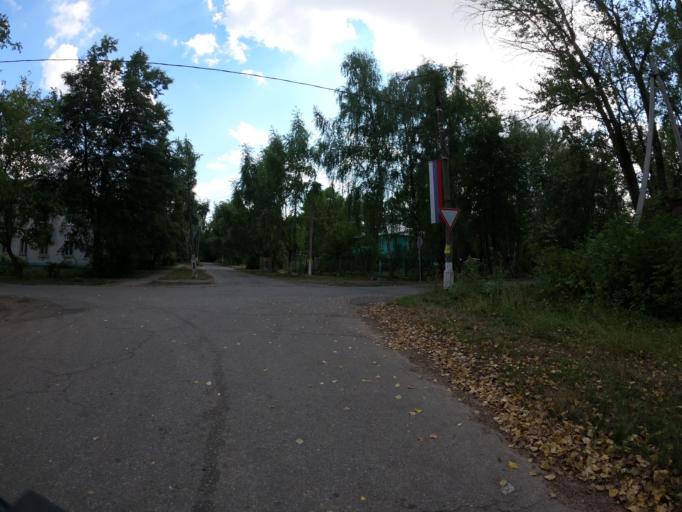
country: RU
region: Moskovskaya
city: Peski
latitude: 55.2688
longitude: 38.7362
